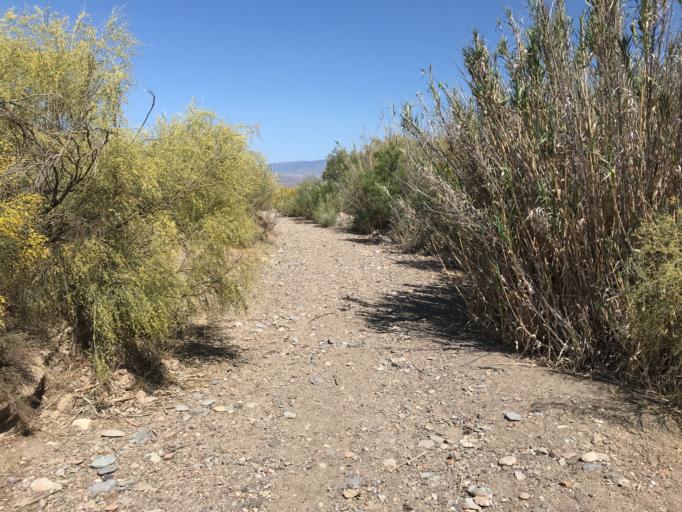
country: ES
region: Andalusia
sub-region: Provincia de Almeria
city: Turrillas
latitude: 37.0677
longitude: -2.2892
